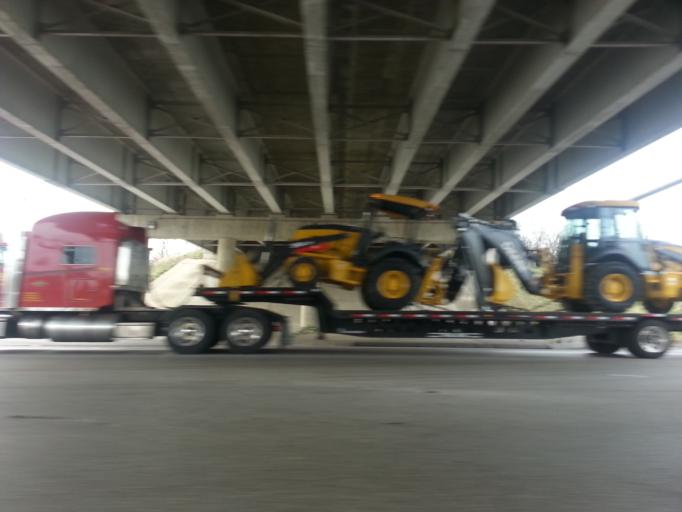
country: US
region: Missouri
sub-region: Marion County
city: Hannibal
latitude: 39.7147
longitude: -91.3920
